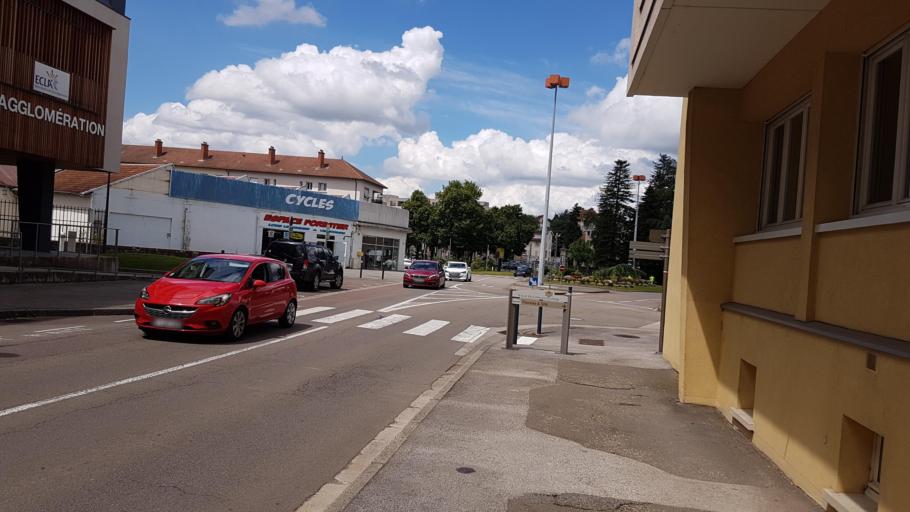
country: FR
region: Franche-Comte
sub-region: Departement du Jura
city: Lons-le-Saunier
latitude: 46.6720
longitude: 5.5590
